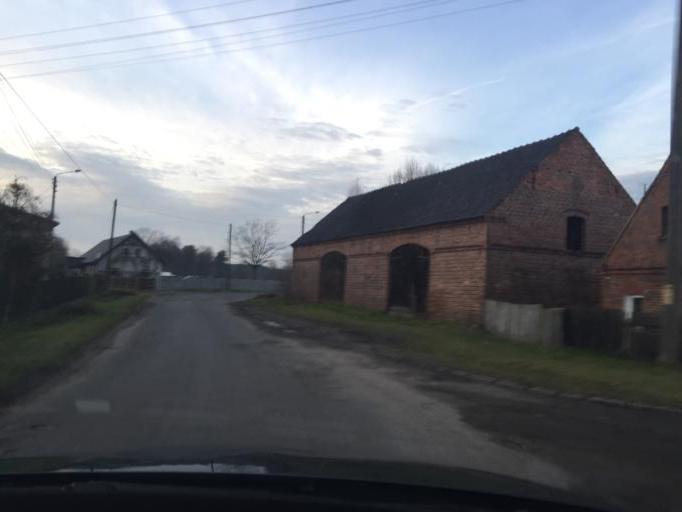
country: PL
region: Lubusz
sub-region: Powiat zielonogorski
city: Ochla
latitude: 51.8078
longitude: 15.4910
